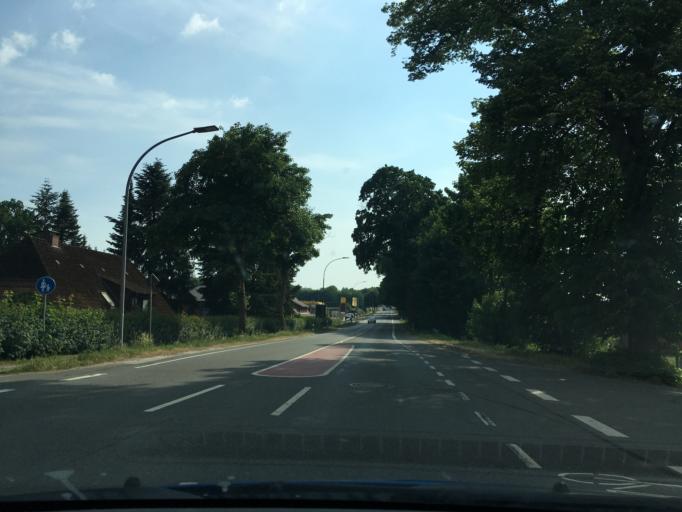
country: DE
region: Lower Saxony
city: Buchholz in der Nordheide
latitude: 53.3786
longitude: 9.8941
